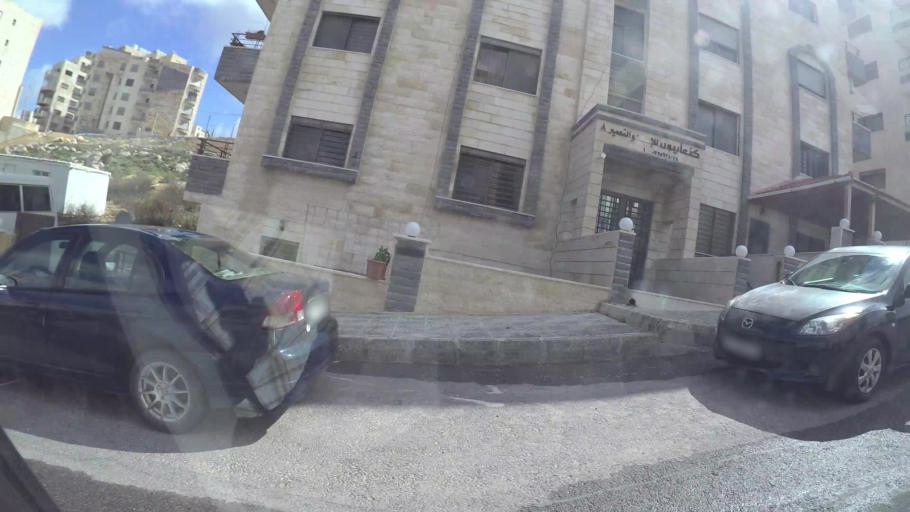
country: JO
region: Amman
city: Al Jubayhah
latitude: 32.0655
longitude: 35.8716
